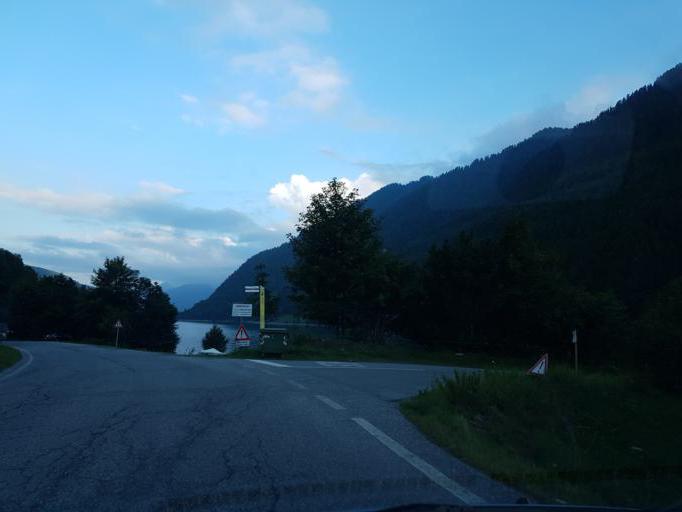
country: IT
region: Piedmont
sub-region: Provincia di Cuneo
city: Pontechianale
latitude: 44.6209
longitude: 7.0322
